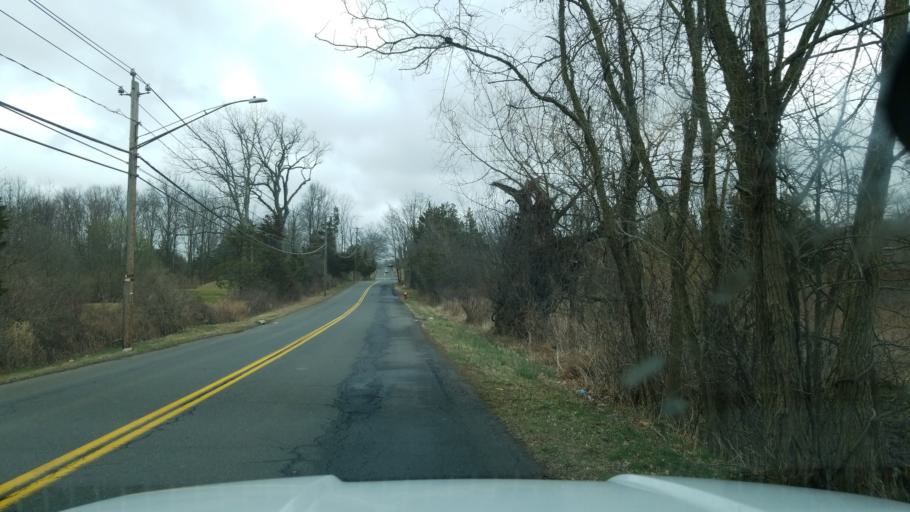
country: US
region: Connecticut
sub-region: Hartford County
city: Kensington
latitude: 41.6015
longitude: -72.7344
